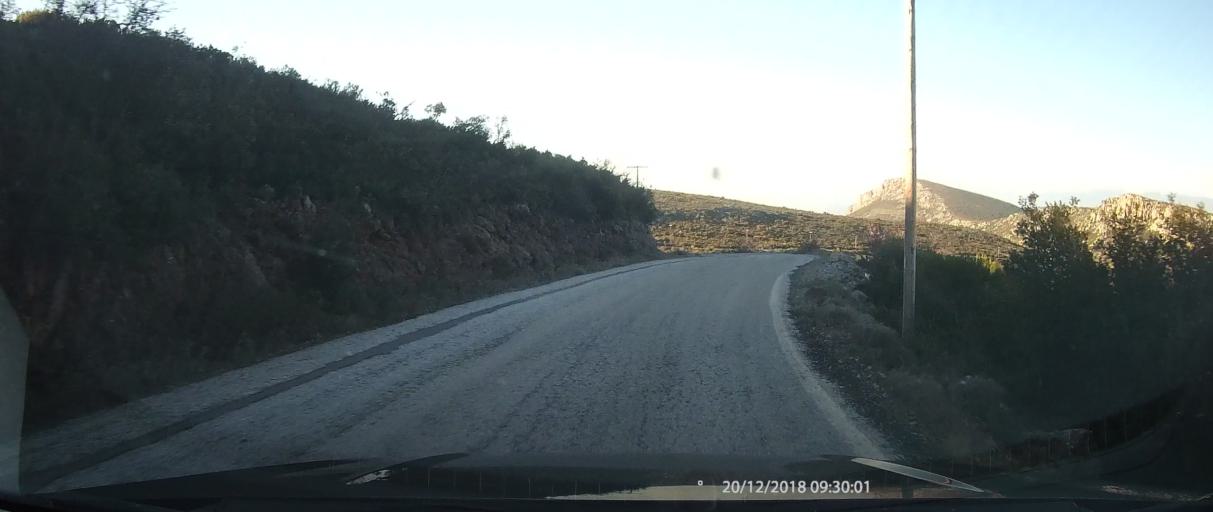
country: GR
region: Peloponnese
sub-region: Nomos Lakonias
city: Kato Glikovrisi
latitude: 36.9558
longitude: 22.8505
